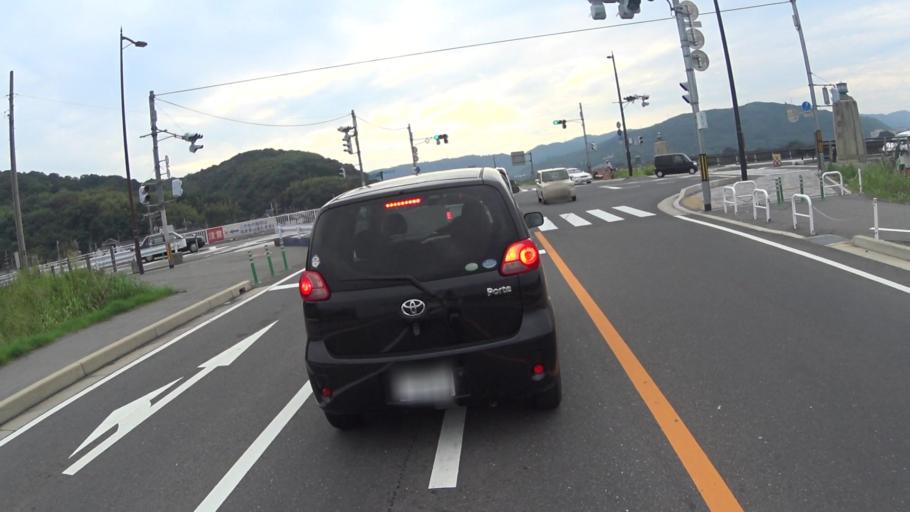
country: JP
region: Kyoto
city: Yawata
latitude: 34.8868
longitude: 135.7009
